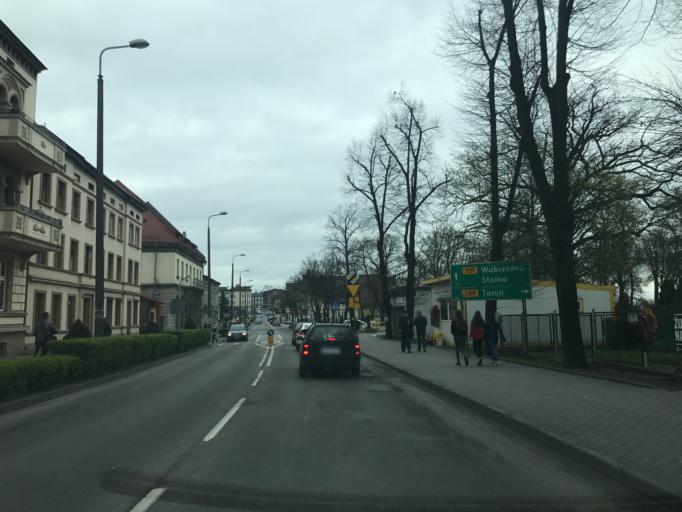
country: PL
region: Kujawsko-Pomorskie
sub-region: Powiat torunski
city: Chelmza
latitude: 53.1836
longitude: 18.6025
